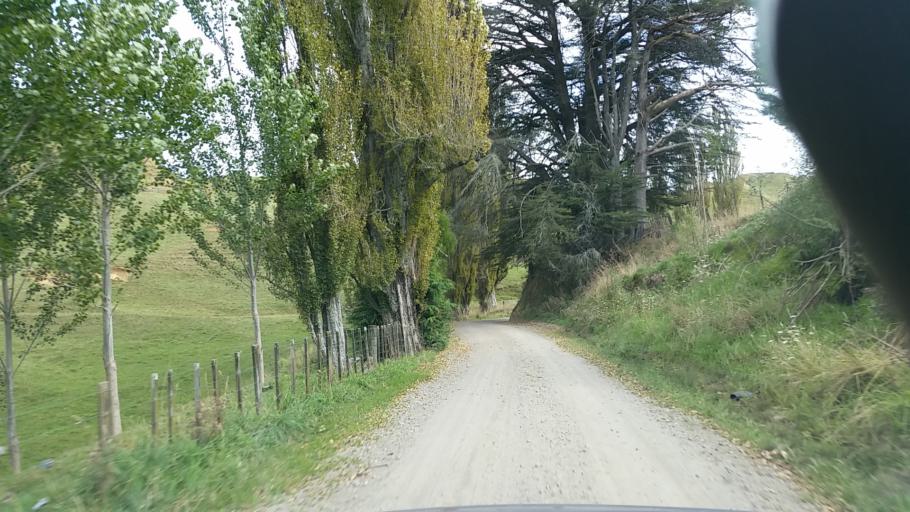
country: NZ
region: Taranaki
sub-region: South Taranaki District
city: Eltham
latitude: -39.2582
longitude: 174.5598
